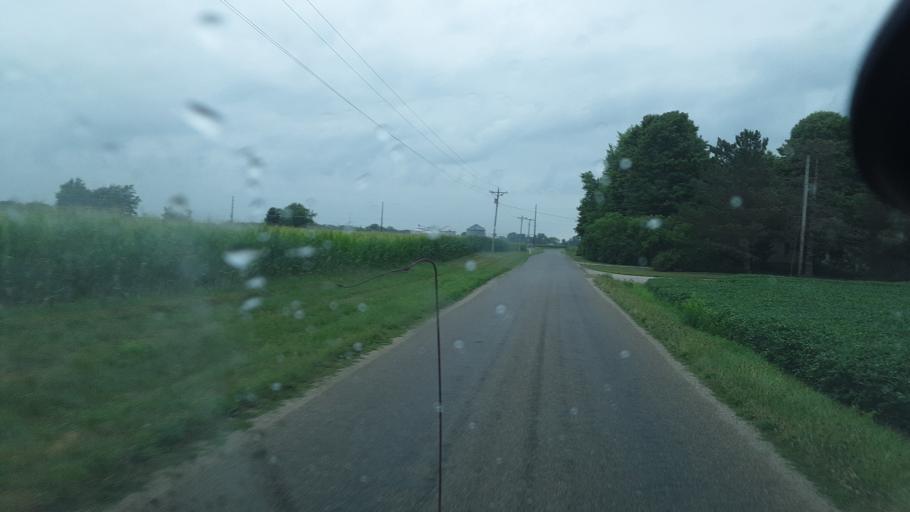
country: US
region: Ohio
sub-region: Defiance County
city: Hicksville
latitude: 41.3368
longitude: -84.6698
